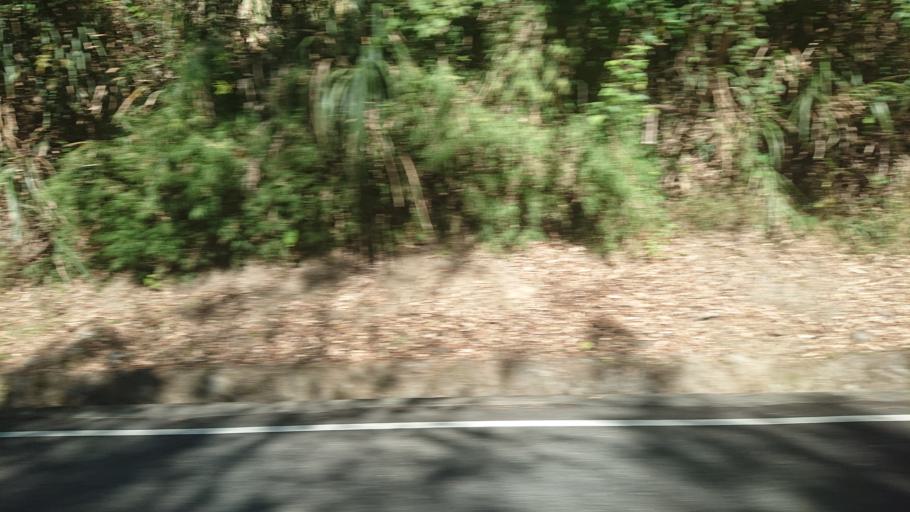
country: TW
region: Taiwan
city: Lugu
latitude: 23.4826
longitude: 120.7379
